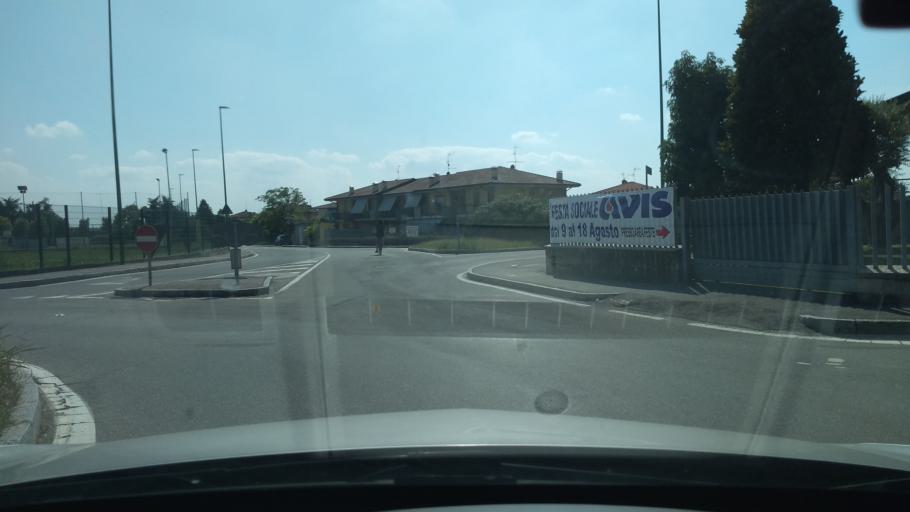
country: IT
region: Lombardy
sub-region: Provincia di Bergamo
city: Ghisalba
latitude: 45.5956
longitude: 9.7517
